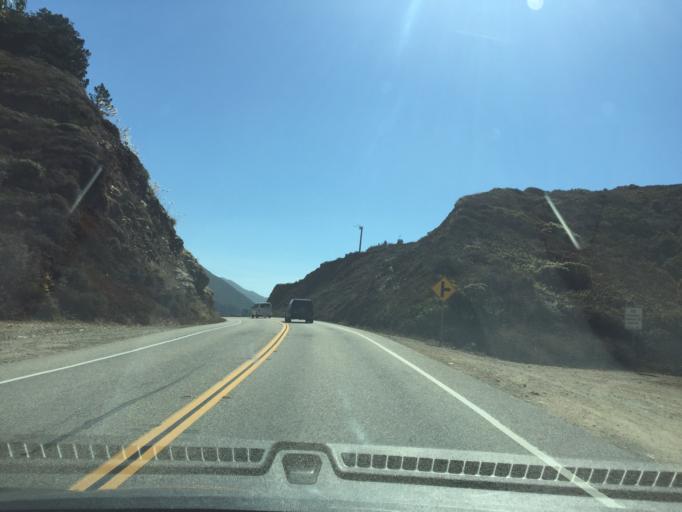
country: US
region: California
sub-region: Monterey County
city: Carmel-by-the-Sea
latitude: 36.4042
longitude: -121.9100
